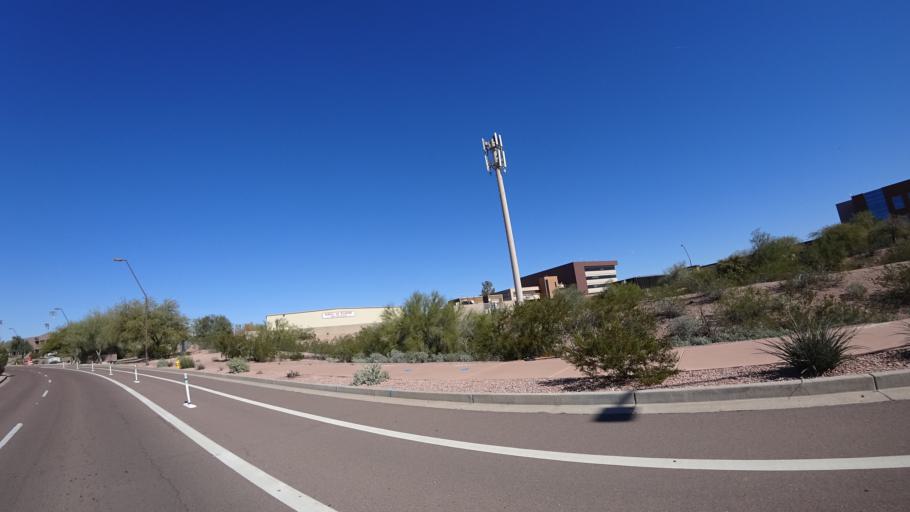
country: US
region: Arizona
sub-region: Maricopa County
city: Tempe Junction
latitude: 33.4454
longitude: -111.9556
